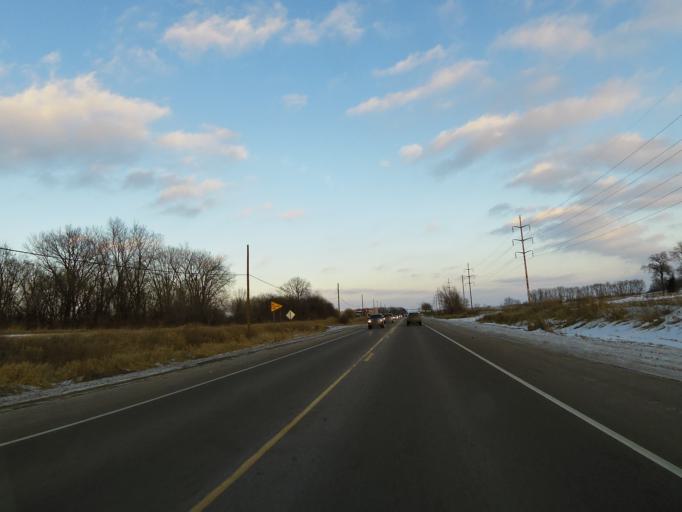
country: US
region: Minnesota
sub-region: Dakota County
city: Lakeville
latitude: 44.6380
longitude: -93.2746
